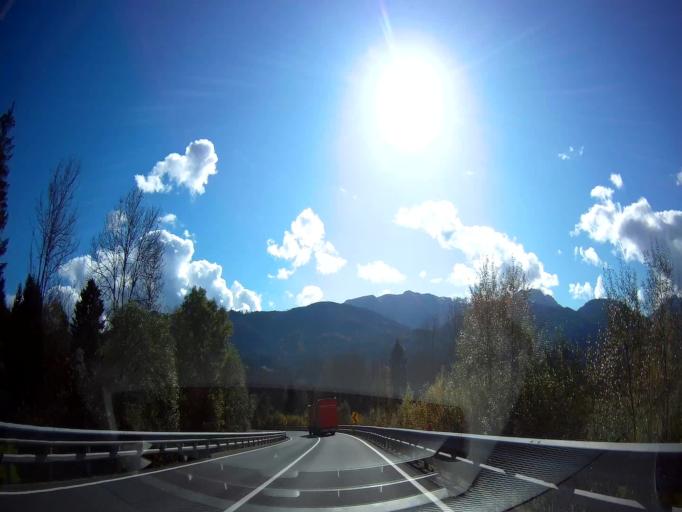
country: AT
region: Carinthia
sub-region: Politischer Bezirk Spittal an der Drau
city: Greifenburg
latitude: 46.7521
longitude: 13.2103
